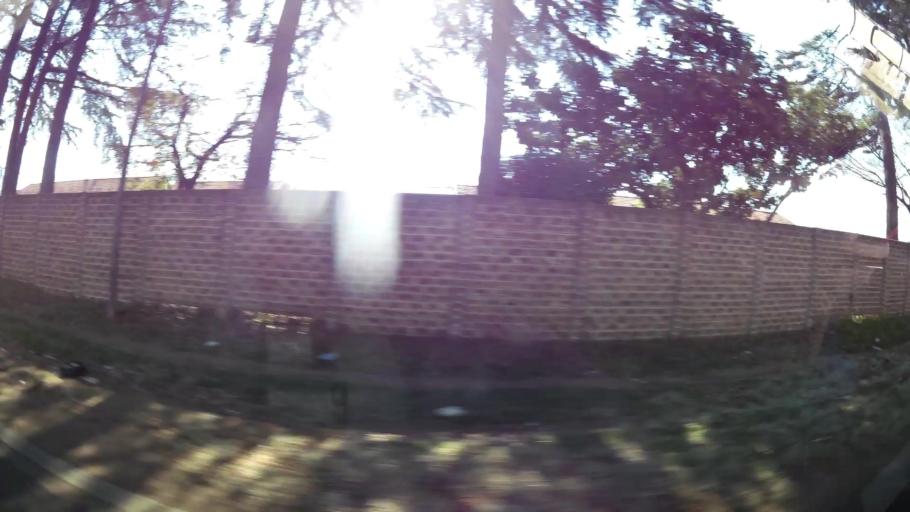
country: ZA
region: Gauteng
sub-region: Ekurhuleni Metropolitan Municipality
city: Boksburg
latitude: -26.1684
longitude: 28.2667
